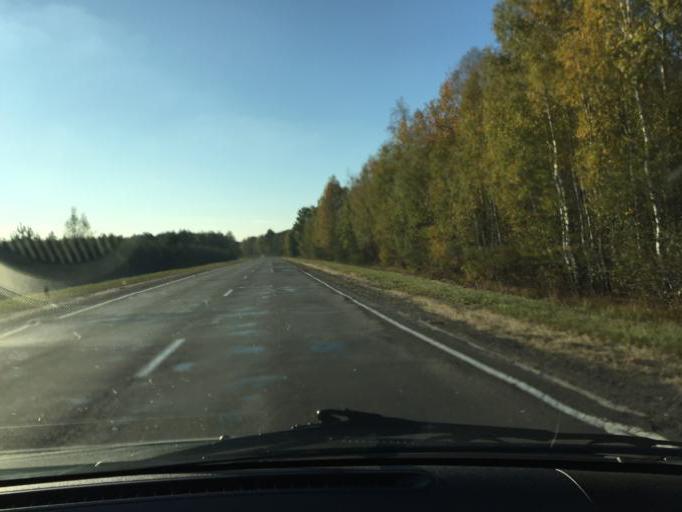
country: BY
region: Brest
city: Horad Luninyets
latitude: 52.3181
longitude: 26.5927
